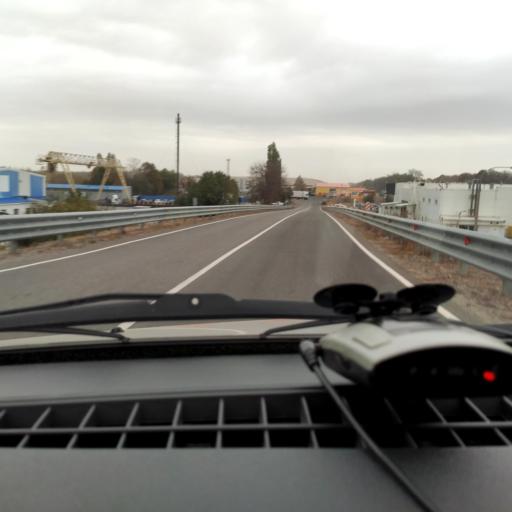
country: RU
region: Voronezj
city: Podgornoye
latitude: 51.7994
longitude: 39.2009
